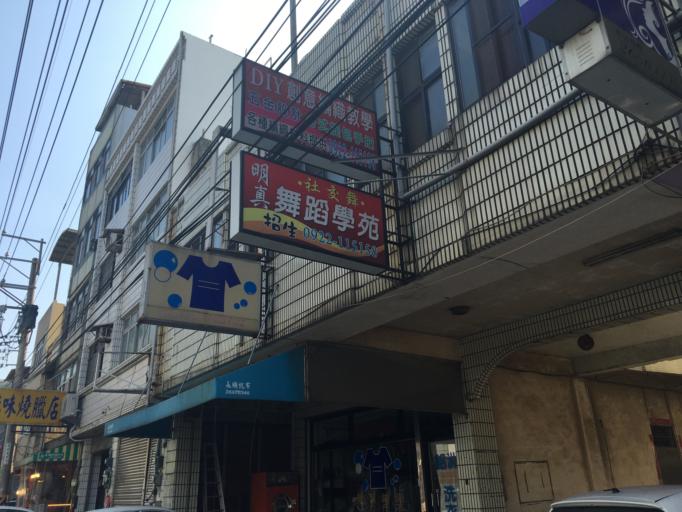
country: TW
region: Taiwan
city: Fengyuan
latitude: 24.3453
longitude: 120.6196
